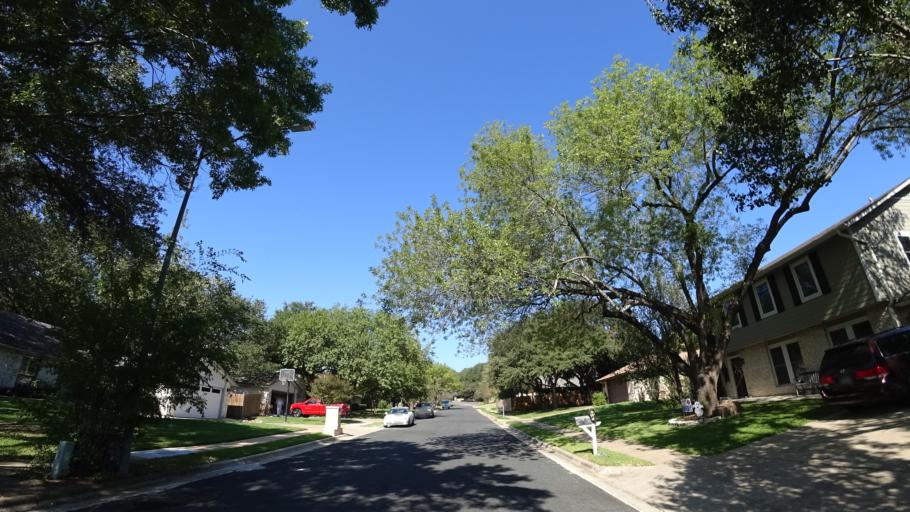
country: US
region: Texas
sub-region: Travis County
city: Rollingwood
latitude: 30.2710
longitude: -97.8066
